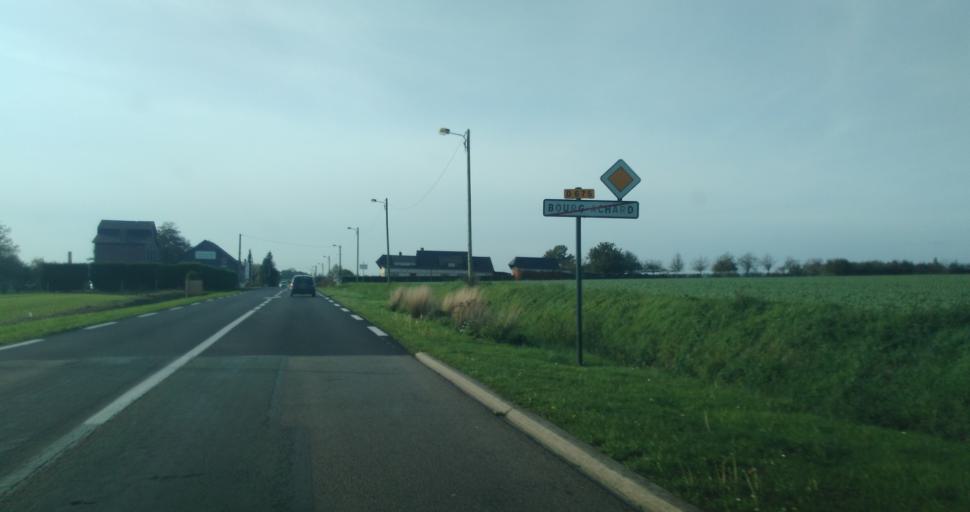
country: FR
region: Haute-Normandie
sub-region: Departement de l'Eure
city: Bourg-Achard
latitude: 49.3557
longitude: 0.7991
